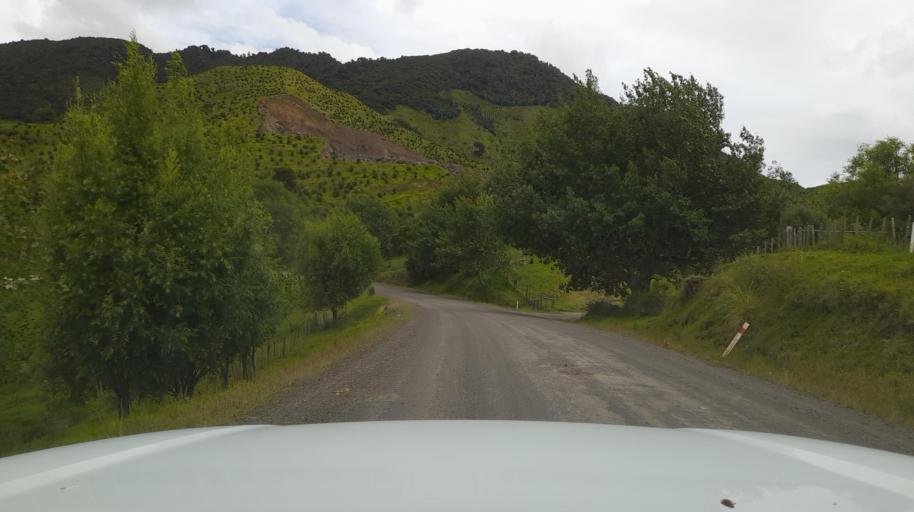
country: NZ
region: Northland
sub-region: Far North District
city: Kaitaia
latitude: -35.3319
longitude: 173.3542
